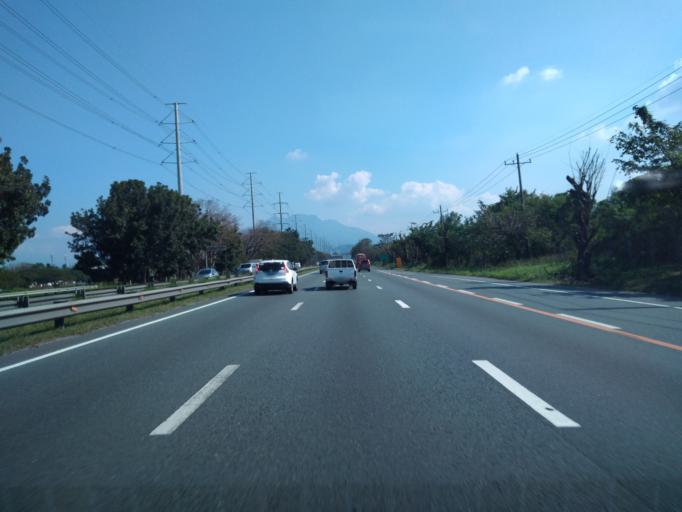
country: PH
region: Calabarzon
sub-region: Province of Laguna
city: Prinza
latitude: 14.2282
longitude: 121.1196
